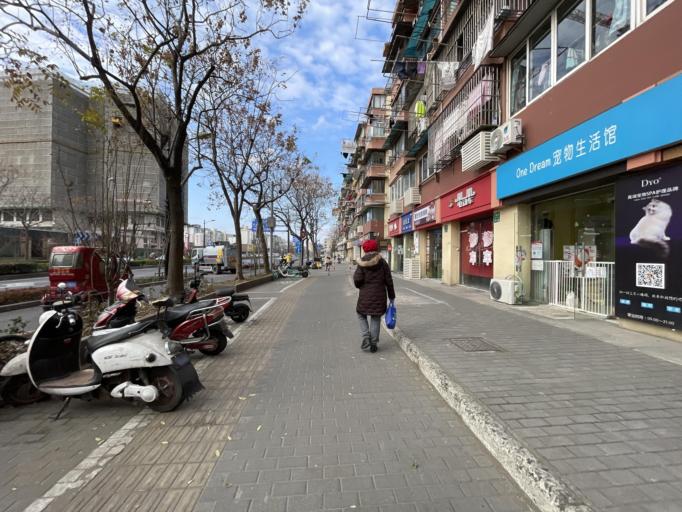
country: CN
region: Shanghai Shi
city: Yangpu
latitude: 31.3101
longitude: 121.4934
